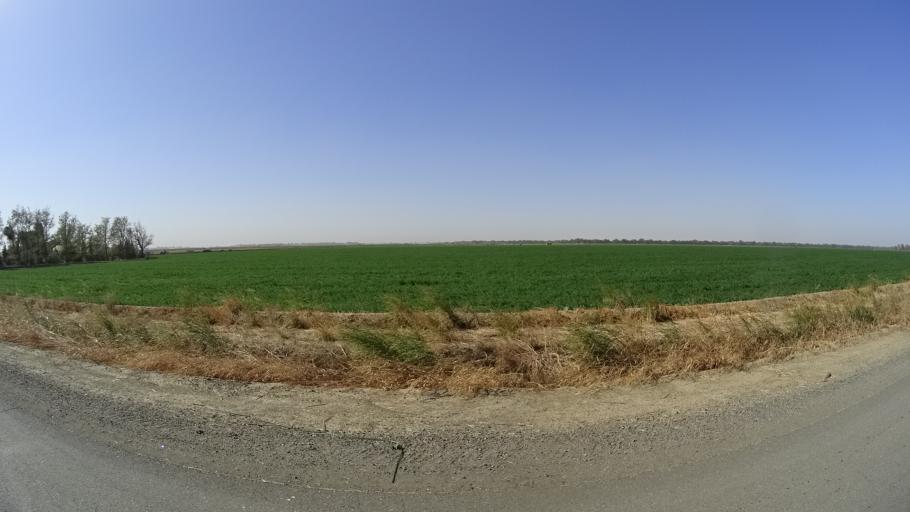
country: US
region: California
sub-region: Yolo County
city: Davis
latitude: 38.5985
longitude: -121.7301
